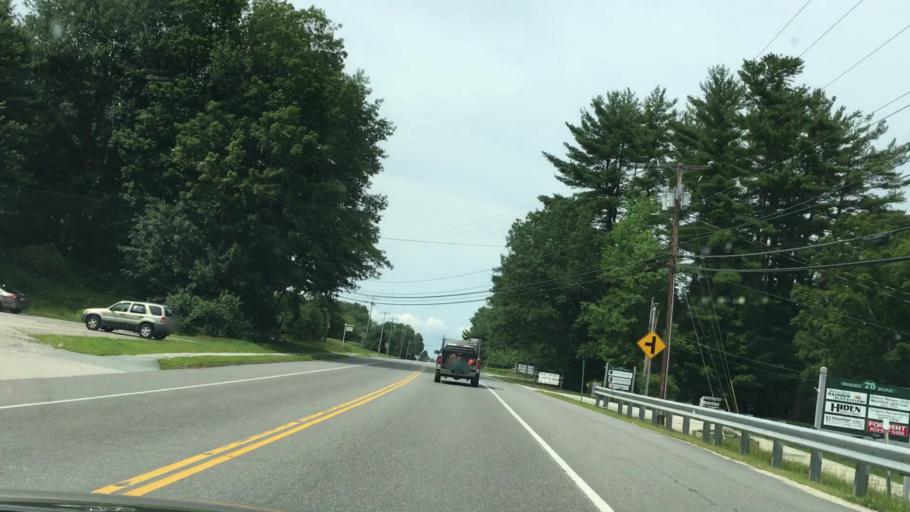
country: US
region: New Hampshire
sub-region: Hillsborough County
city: Peterborough
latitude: 42.9040
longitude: -71.9367
